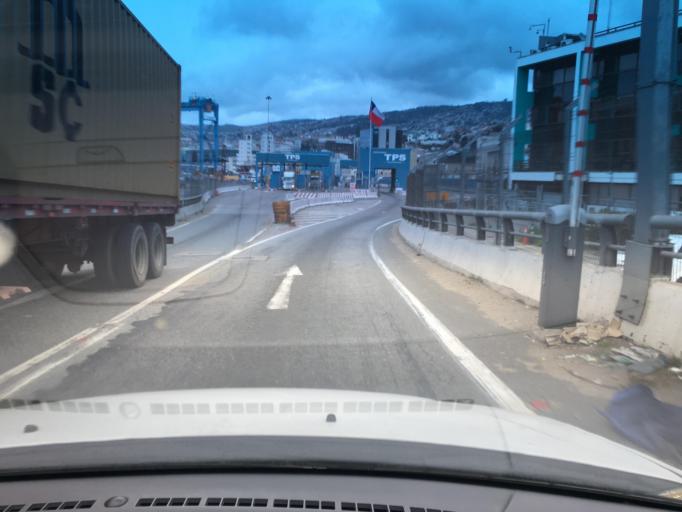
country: CL
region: Valparaiso
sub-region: Provincia de Valparaiso
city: Valparaiso
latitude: -33.0338
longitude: -71.6291
